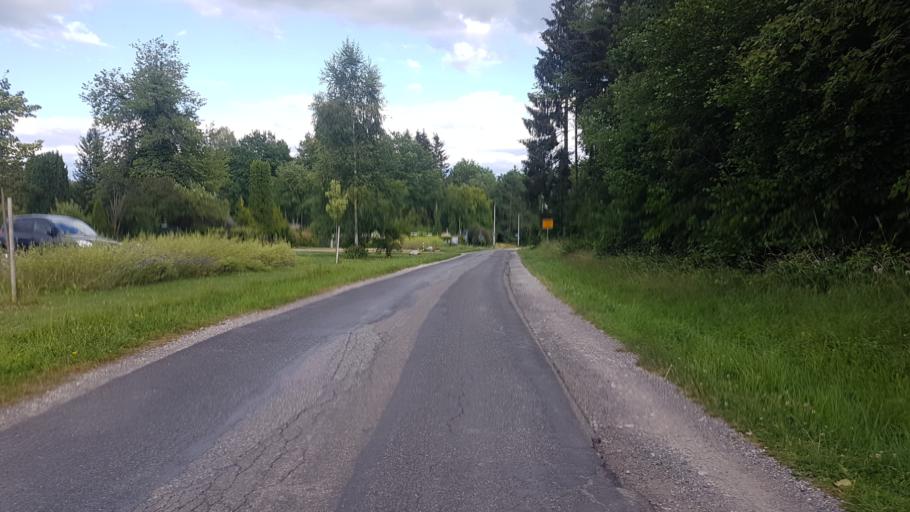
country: DE
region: Baden-Wuerttemberg
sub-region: Freiburg Region
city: Monchweiler
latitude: 48.0618
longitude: 8.4230
